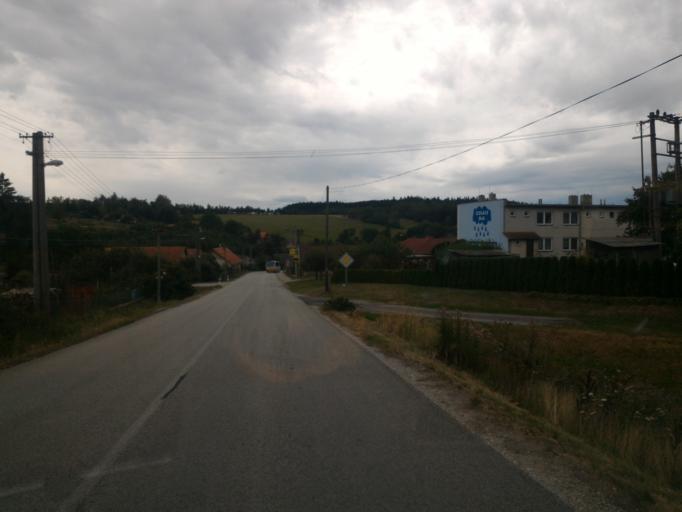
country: CZ
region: Vysocina
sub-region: Okres Jihlava
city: Trest'
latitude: 49.2280
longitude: 15.5373
